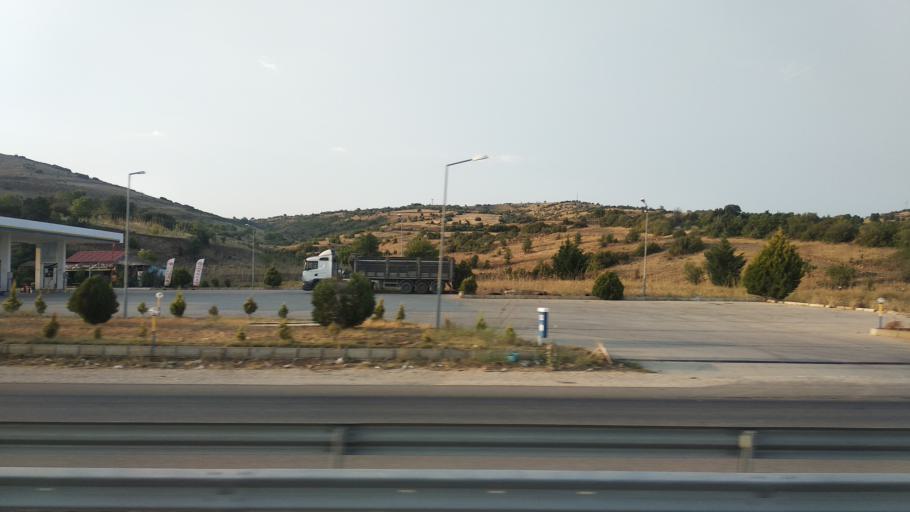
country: TR
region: Manisa
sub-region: Kula
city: Kula
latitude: 38.5677
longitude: 28.5719
